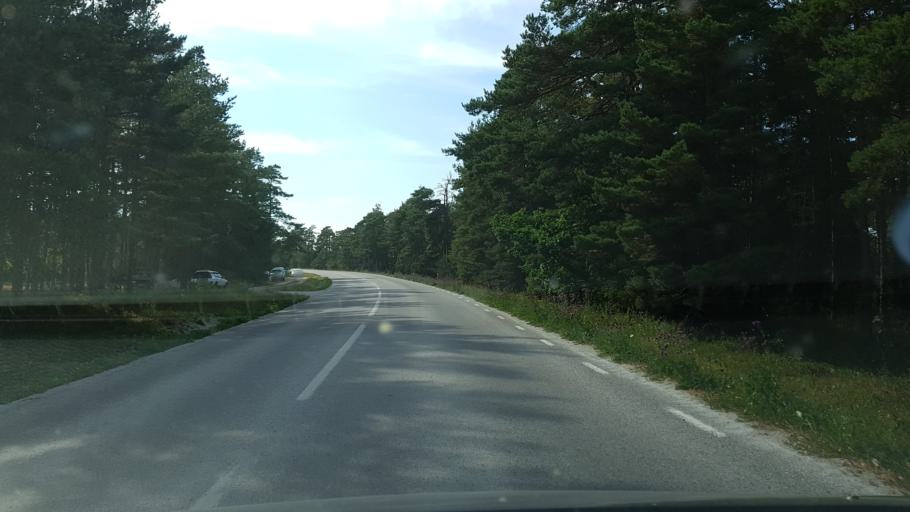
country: SE
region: Gotland
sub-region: Gotland
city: Visby
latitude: 57.6374
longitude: 18.4002
